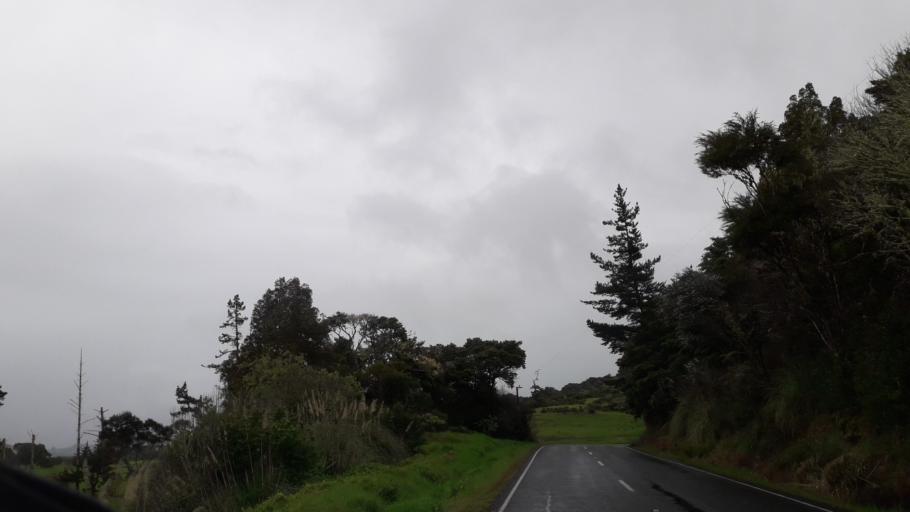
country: NZ
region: Northland
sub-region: Far North District
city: Kaitaia
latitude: -35.3621
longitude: 173.4951
